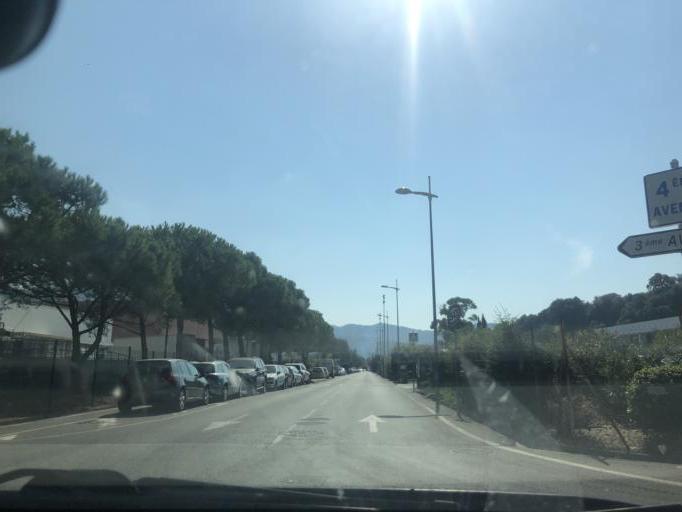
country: FR
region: Provence-Alpes-Cote d'Azur
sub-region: Departement des Alpes-Maritimes
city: Carros
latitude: 43.7947
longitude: 7.2012
